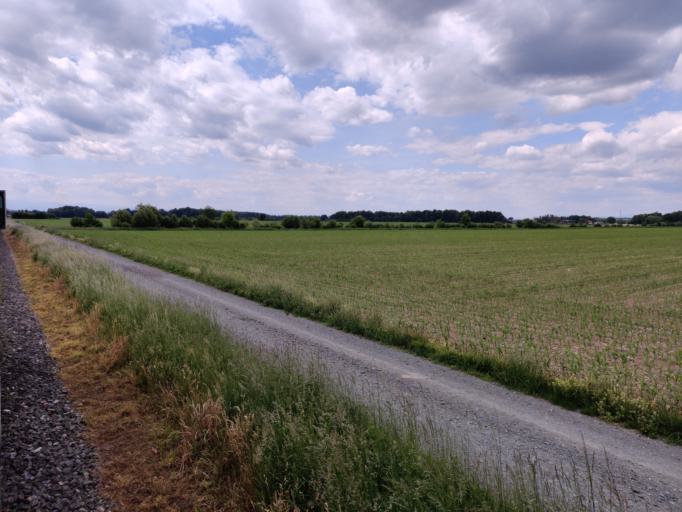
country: SI
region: Sentilj
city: Selnica ob Muri
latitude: 46.7141
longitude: 15.6967
